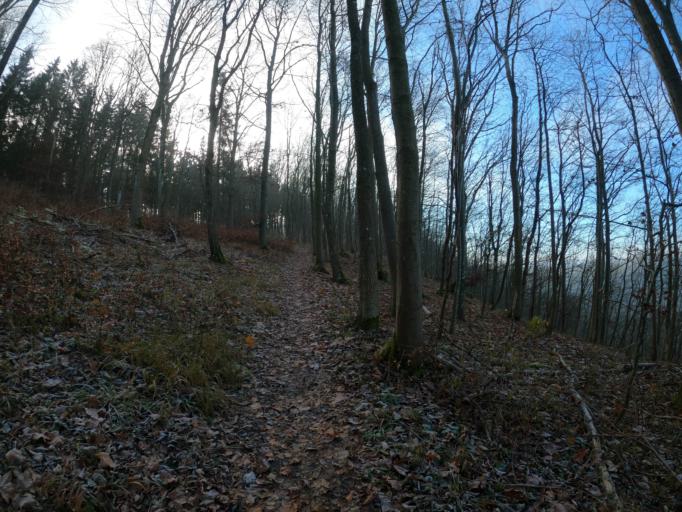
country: DE
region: Baden-Wuerttemberg
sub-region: Regierungsbezirk Stuttgart
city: Deggingen
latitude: 48.5906
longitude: 9.7400
